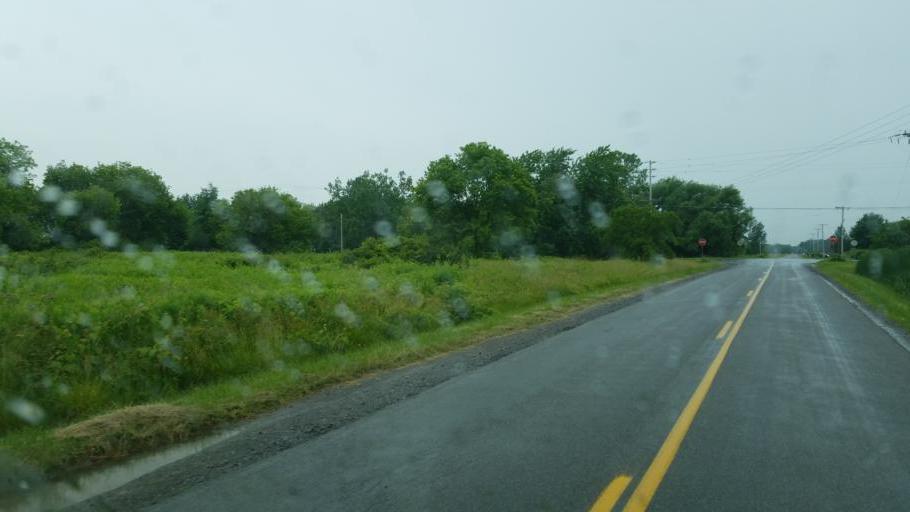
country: US
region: New York
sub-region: Niagara County
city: Ransomville
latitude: 43.2641
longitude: -78.8690
